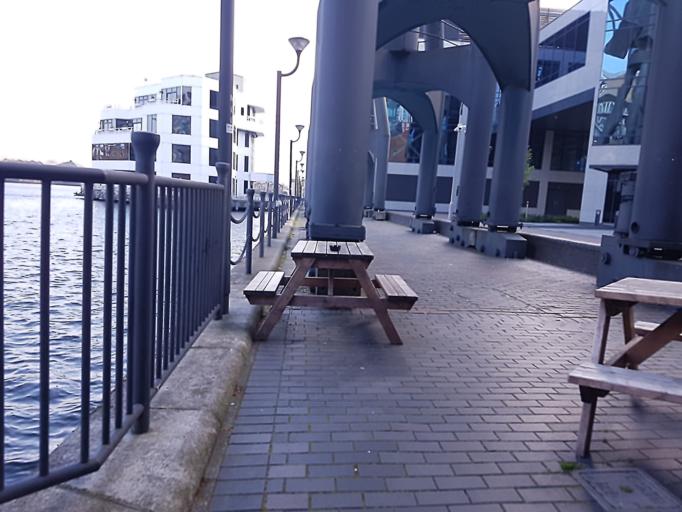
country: GB
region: England
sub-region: Greater London
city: Poplar
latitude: 51.4962
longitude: -0.0177
